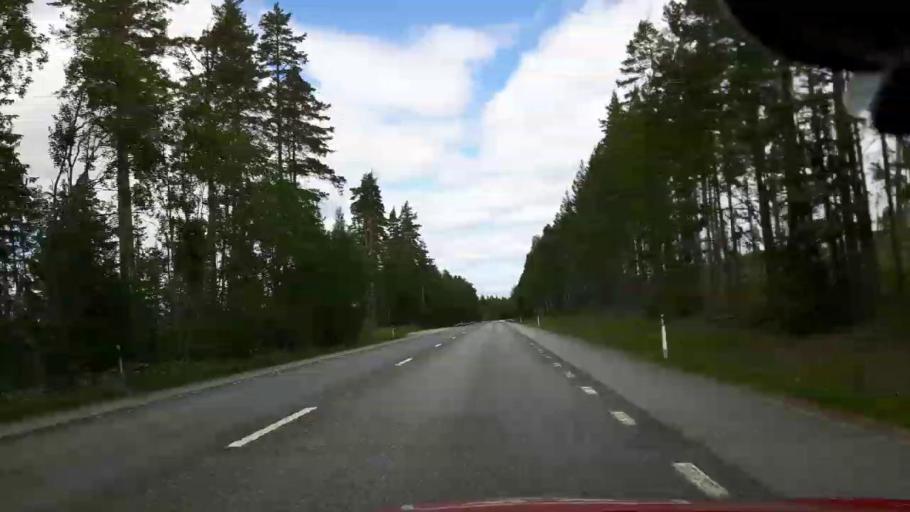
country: SE
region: Jaemtland
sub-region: Braecke Kommun
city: Braecke
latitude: 62.7253
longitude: 15.4431
